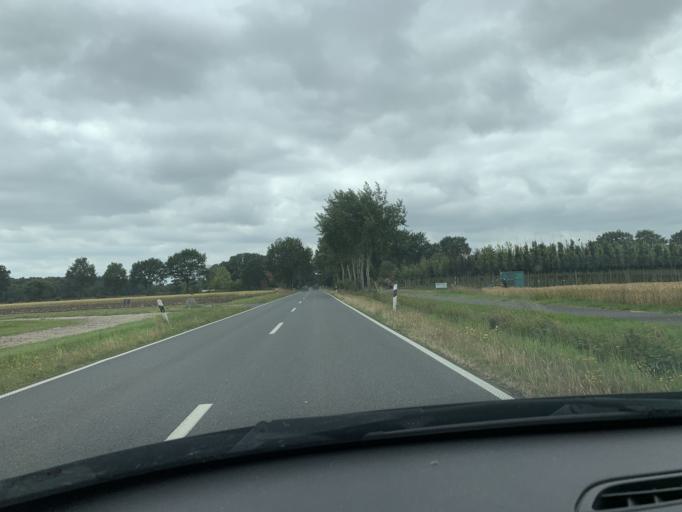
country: DE
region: Lower Saxony
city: Bad Zwischenahn
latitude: 53.2262
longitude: 7.9836
